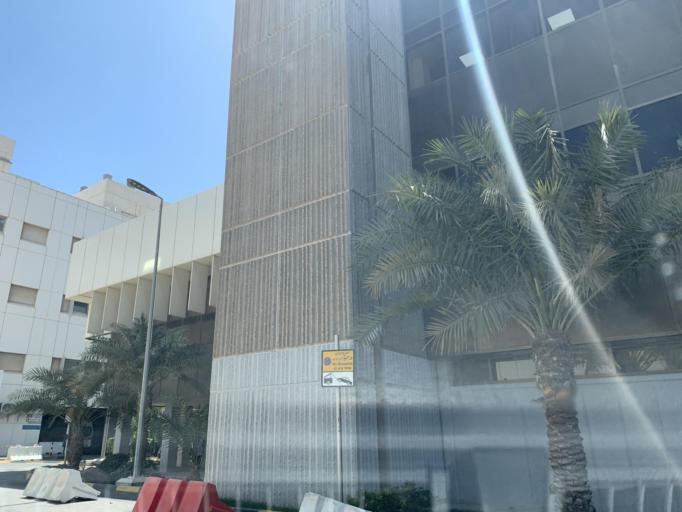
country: BH
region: Manama
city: Manama
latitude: 26.2166
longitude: 50.5713
